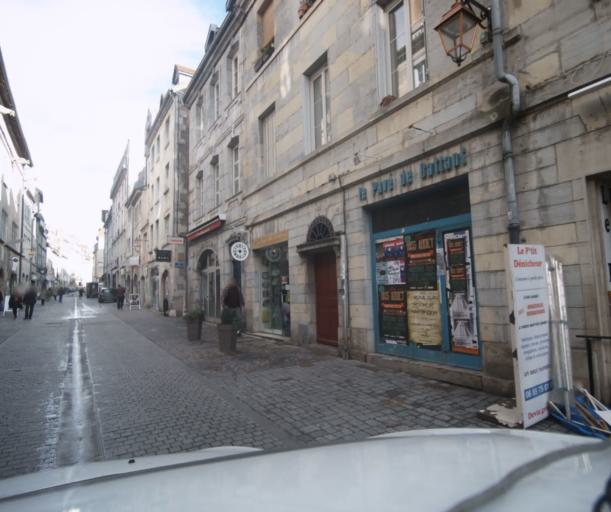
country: FR
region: Franche-Comte
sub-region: Departement du Doubs
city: Besancon
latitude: 47.2412
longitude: 6.0204
